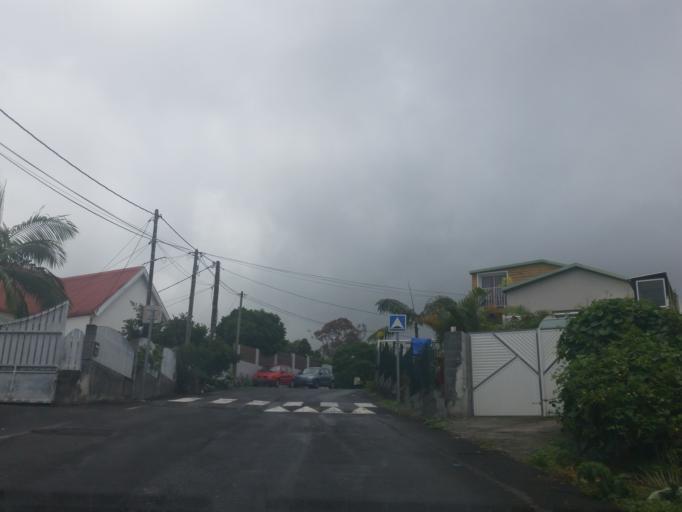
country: RE
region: Reunion
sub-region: Reunion
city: Le Tampon
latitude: -21.2421
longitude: 55.5142
